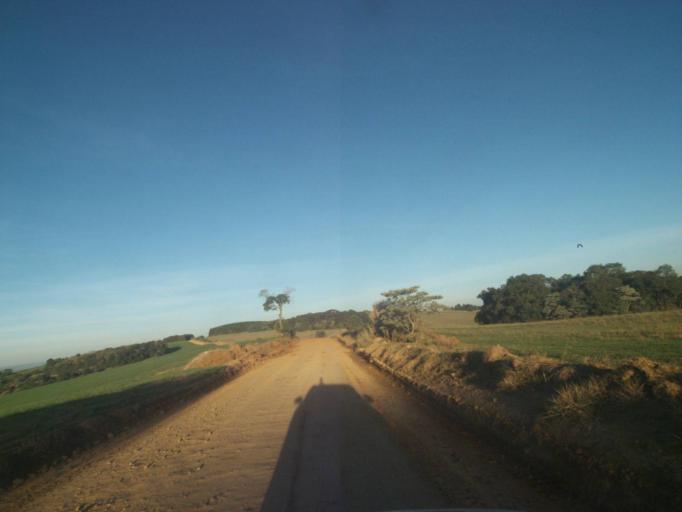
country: BR
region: Parana
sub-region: Tibagi
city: Tibagi
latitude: -24.5449
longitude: -50.5487
